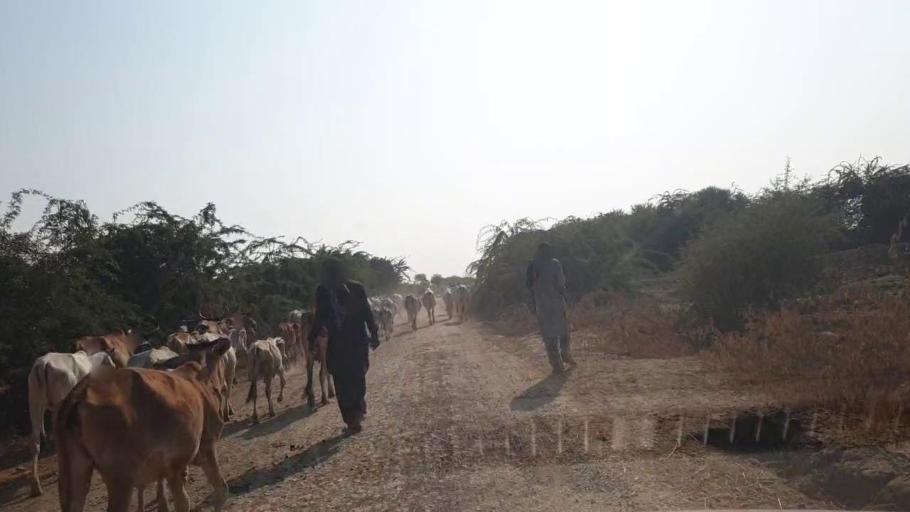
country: PK
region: Sindh
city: Matli
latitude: 24.9477
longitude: 68.6835
